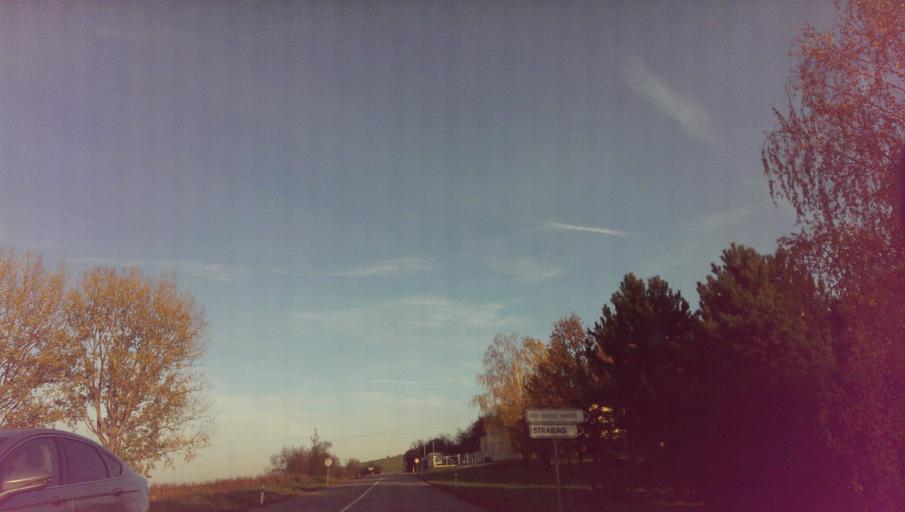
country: CZ
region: Zlin
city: Knezpole
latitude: 49.0910
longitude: 17.5137
